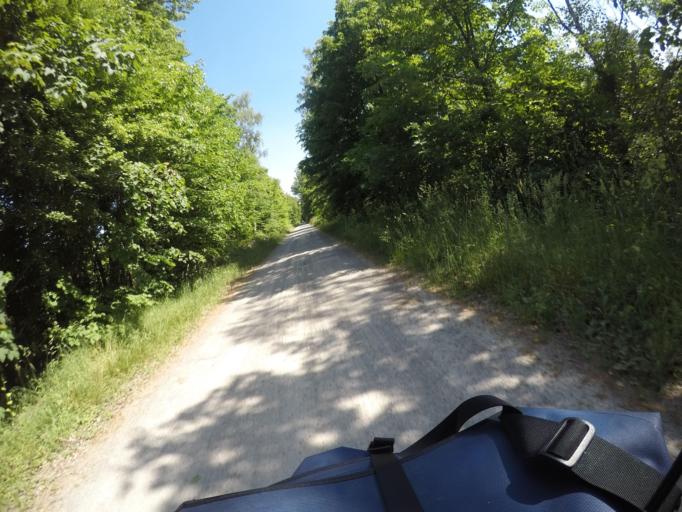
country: DE
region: Baden-Wuerttemberg
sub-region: Karlsruhe Region
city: Rheinstetten
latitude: 48.9559
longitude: 8.3285
